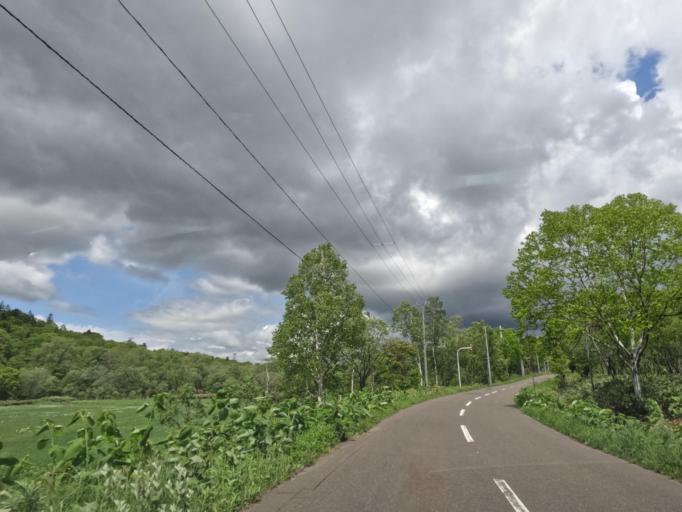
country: JP
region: Hokkaido
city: Tobetsu
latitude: 43.4486
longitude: 141.5849
